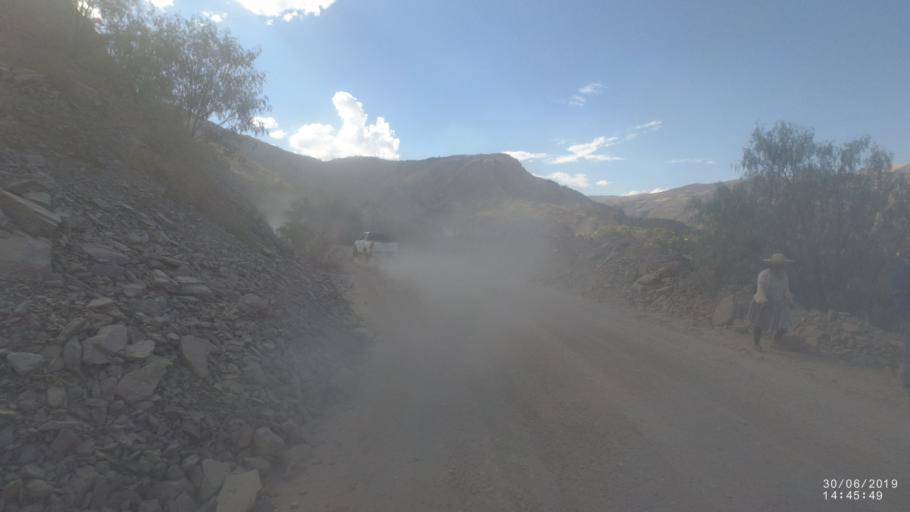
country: BO
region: Cochabamba
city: Irpa Irpa
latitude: -17.7967
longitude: -66.3502
